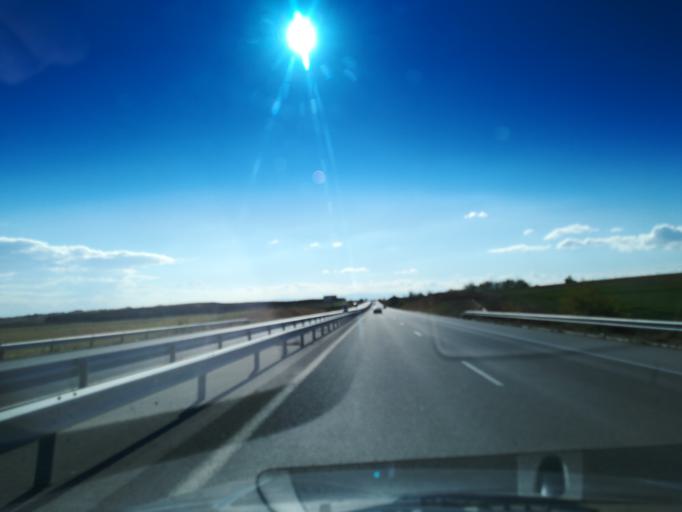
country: BG
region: Stara Zagora
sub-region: Obshtina Nikolaevo
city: Elkhovo
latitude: 42.2682
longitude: 25.4405
